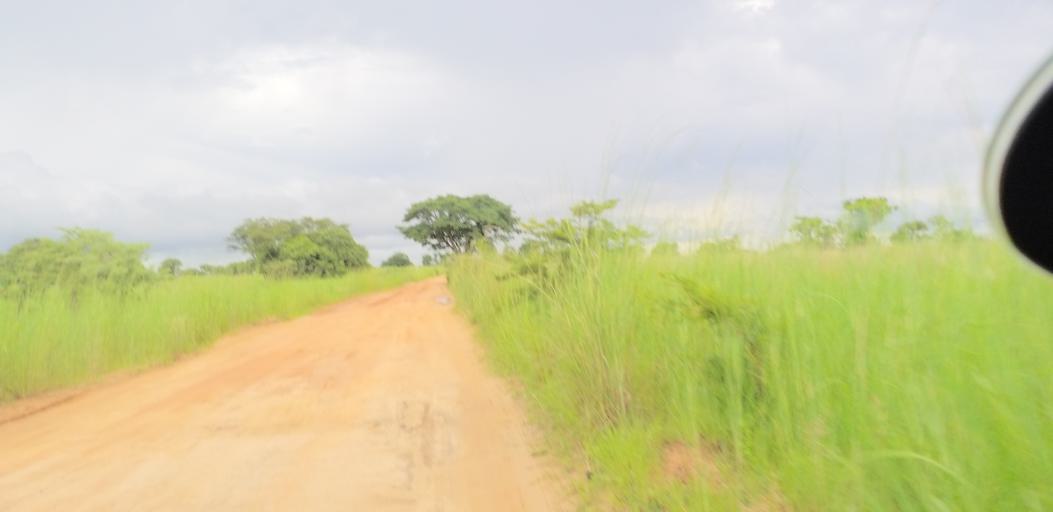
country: ZM
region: Lusaka
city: Chongwe
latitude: -15.1678
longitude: 28.4701
